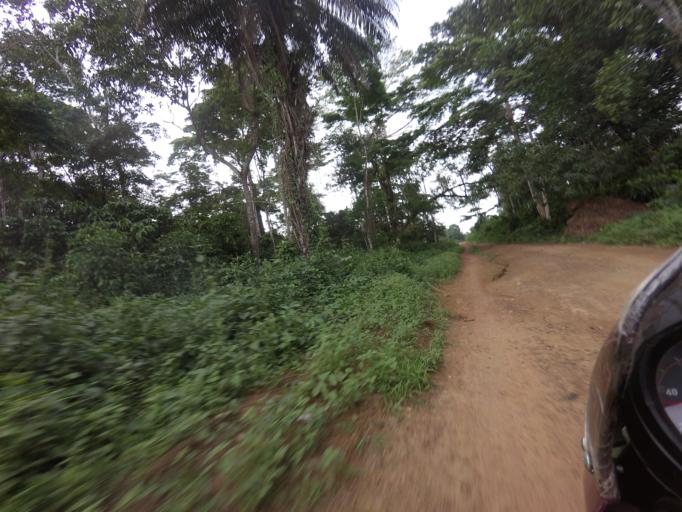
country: SL
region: Eastern Province
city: Jojoima
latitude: 7.7948
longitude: -10.8131
